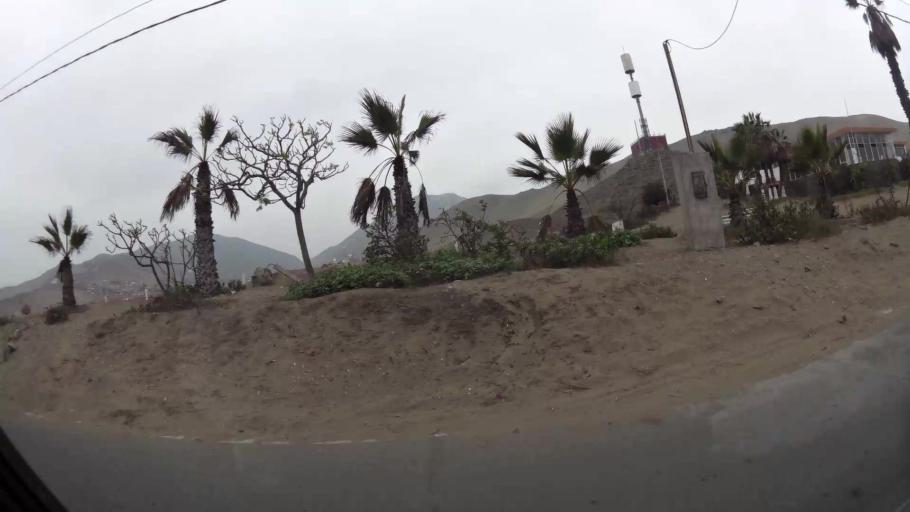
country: PE
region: Lima
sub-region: Lima
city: Santa Rosa
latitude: -11.8027
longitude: -77.1726
